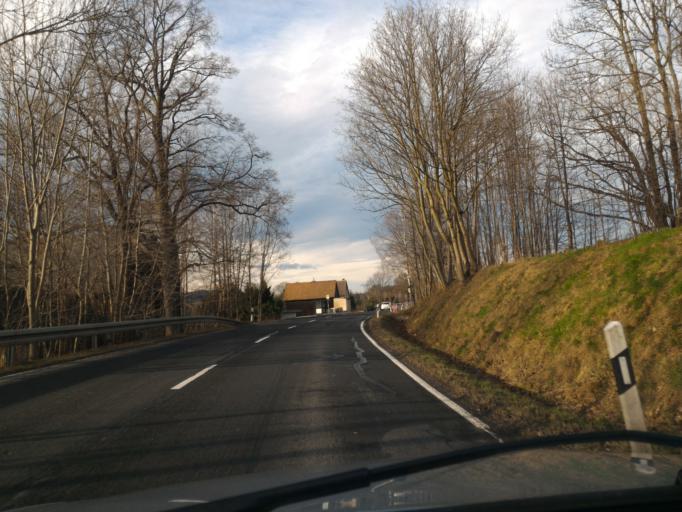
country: DE
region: Saxony
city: Demitz-Thumitz
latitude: 51.0993
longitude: 14.2505
